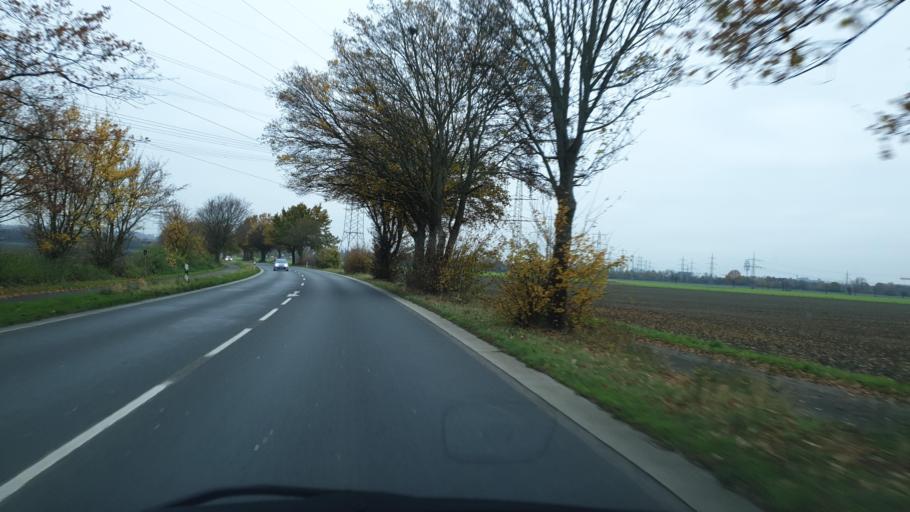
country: DE
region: North Rhine-Westphalia
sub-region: Regierungsbezirk Koln
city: Frechen
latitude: 50.9027
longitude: 6.8406
